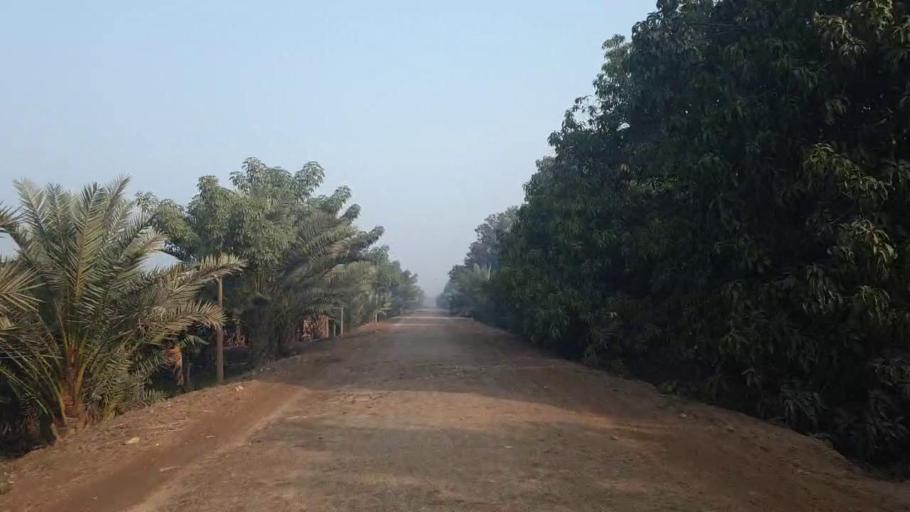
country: PK
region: Sindh
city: Tando Adam
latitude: 25.7885
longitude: 68.6403
